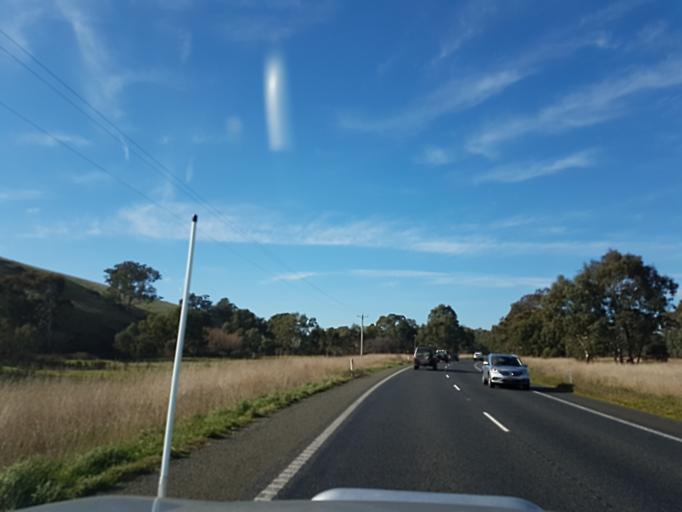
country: AU
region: Victoria
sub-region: Murrindindi
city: Alexandra
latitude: -37.1543
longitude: 145.5693
